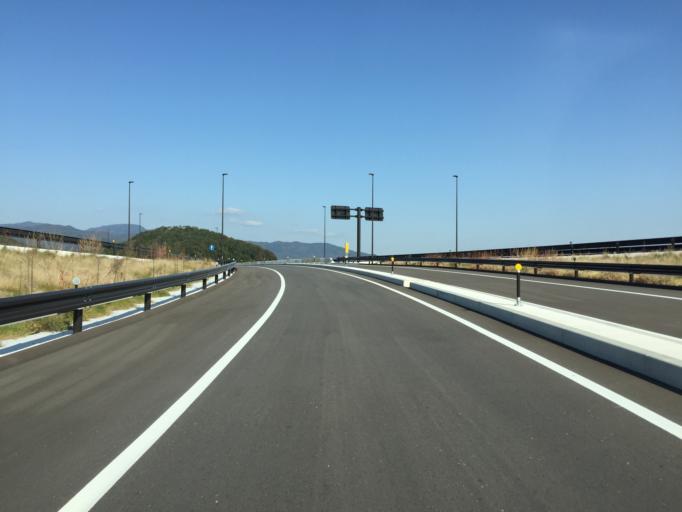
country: JP
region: Fukushima
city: Fukushima-shi
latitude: 37.8020
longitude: 140.4117
